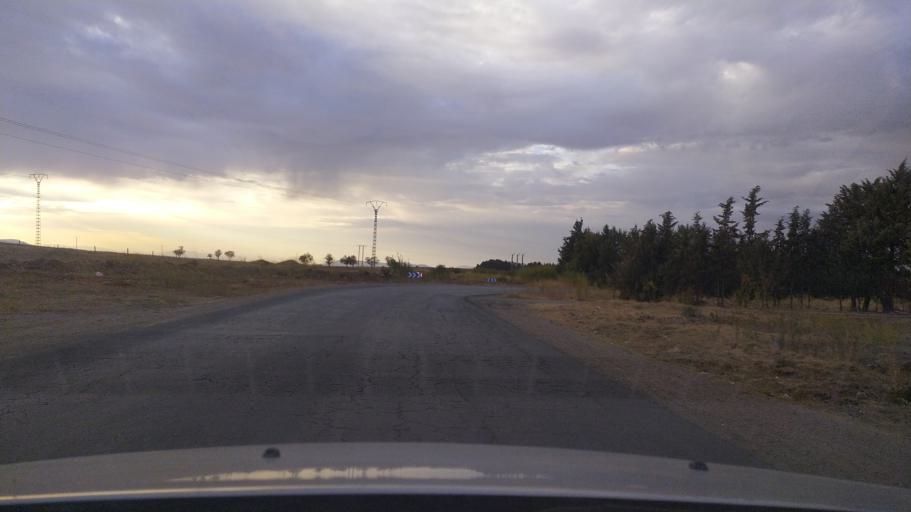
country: DZ
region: Tiaret
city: Frenda
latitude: 35.0306
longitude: 1.0927
